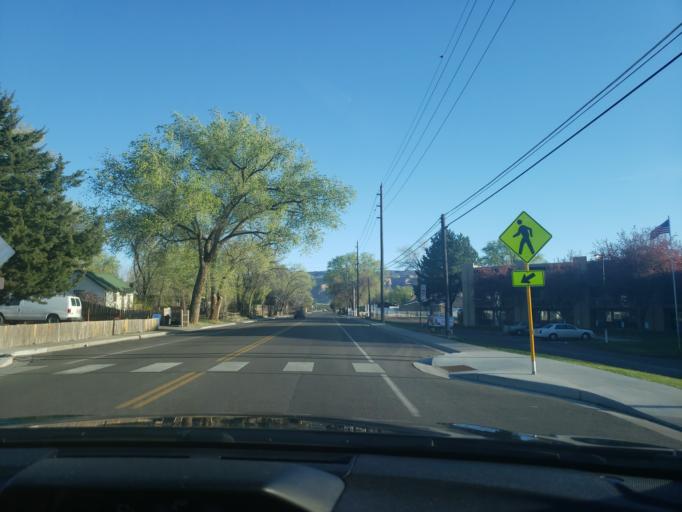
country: US
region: Colorado
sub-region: Mesa County
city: Fruita
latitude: 39.1621
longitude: -108.7384
